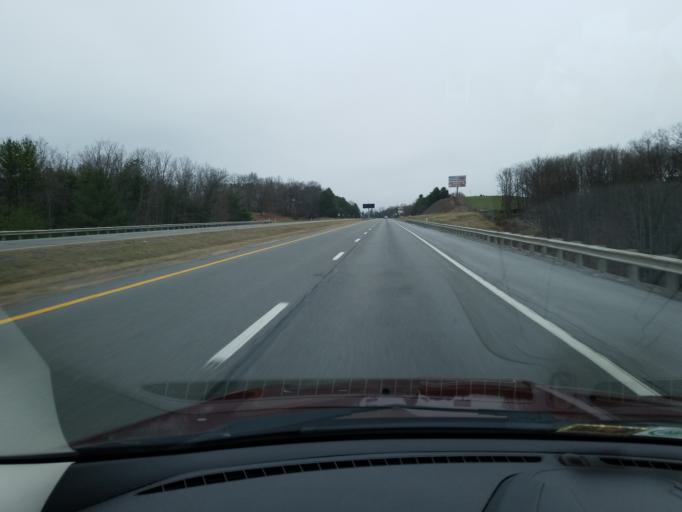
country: US
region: West Virginia
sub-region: Mercer County
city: Athens
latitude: 37.3591
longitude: -81.0260
